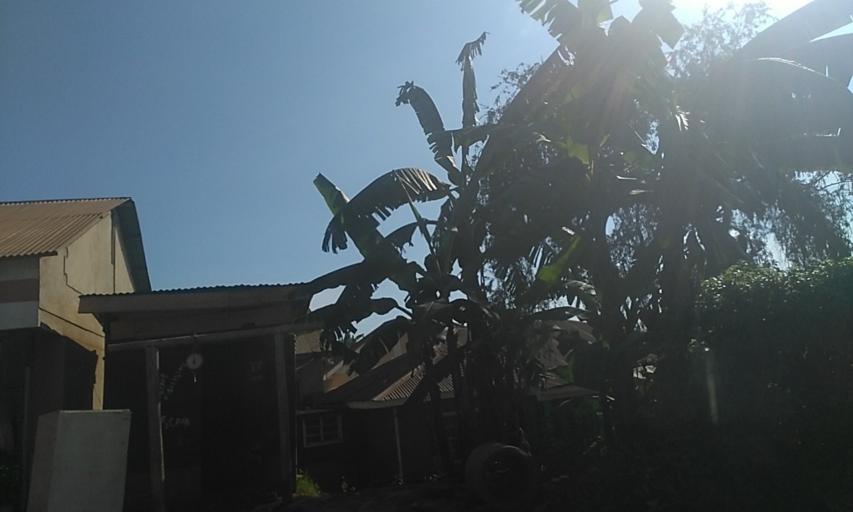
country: UG
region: Central Region
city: Kampala Central Division
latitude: 0.3193
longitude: 32.5484
